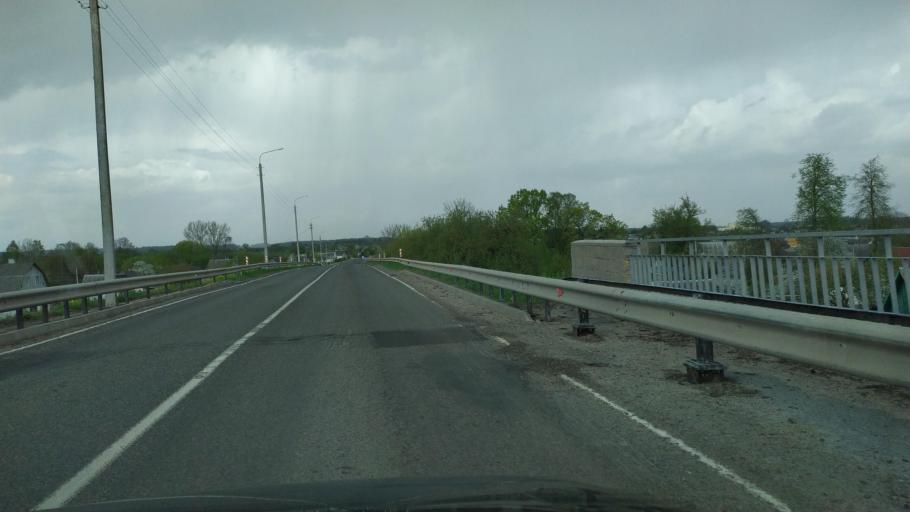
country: BY
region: Brest
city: Pruzhany
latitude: 52.4686
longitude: 24.5159
